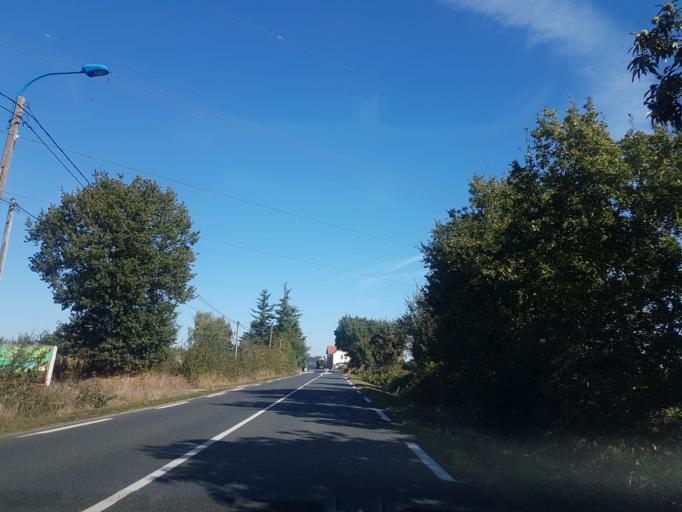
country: FR
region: Pays de la Loire
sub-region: Departement de la Loire-Atlantique
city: Nort-sur-Erdre
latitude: 47.4215
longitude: -1.4837
